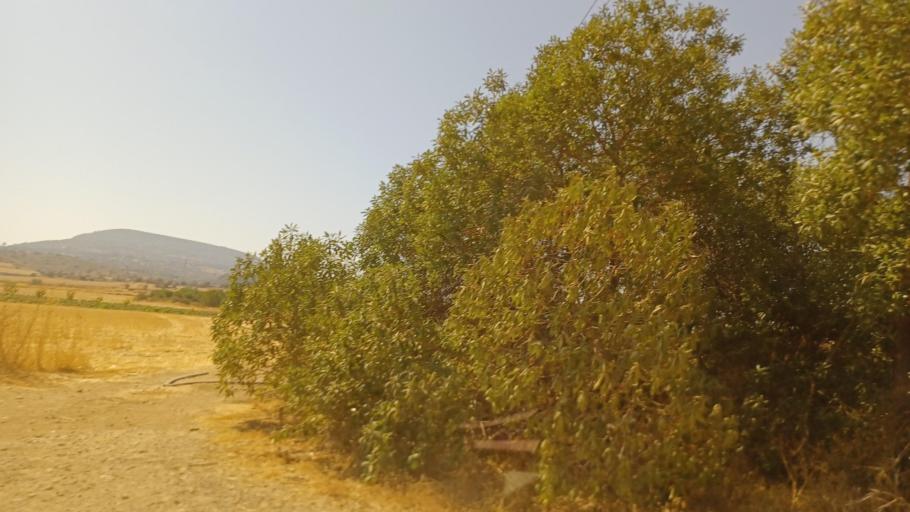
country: CY
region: Pafos
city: Polis
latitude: 35.0472
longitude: 32.4556
